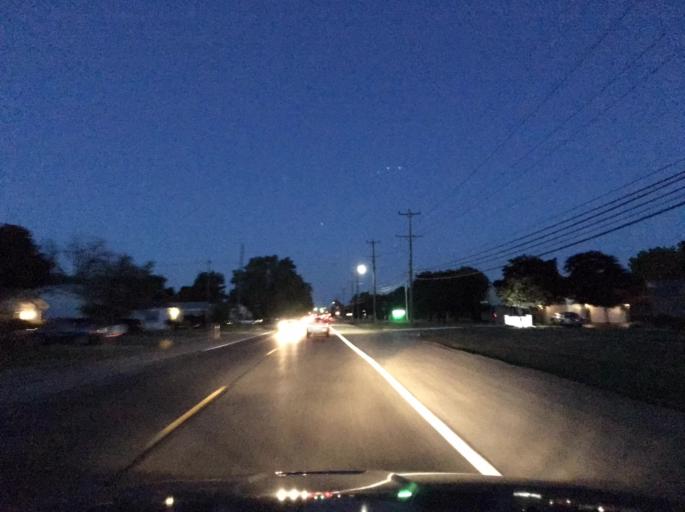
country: US
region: Michigan
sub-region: Macomb County
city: Fraser
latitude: 42.5394
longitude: -82.9233
